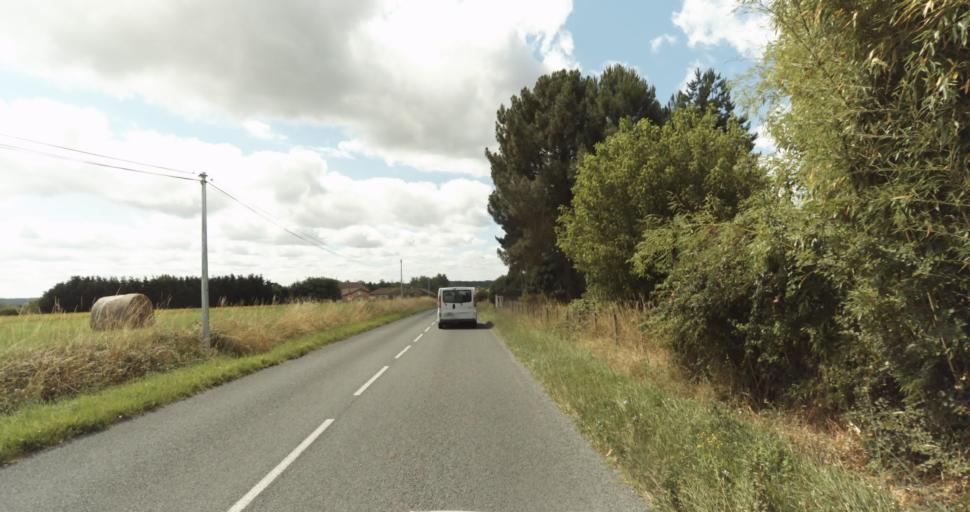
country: FR
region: Aquitaine
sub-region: Departement de la Gironde
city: Bazas
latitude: 44.4432
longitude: -0.2065
